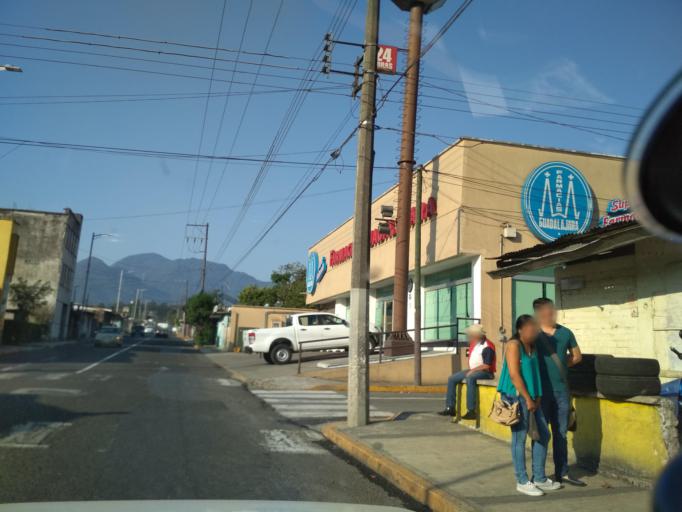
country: MX
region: Veracruz
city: Ixtac Zoquitlan
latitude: 18.8601
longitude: -97.0783
